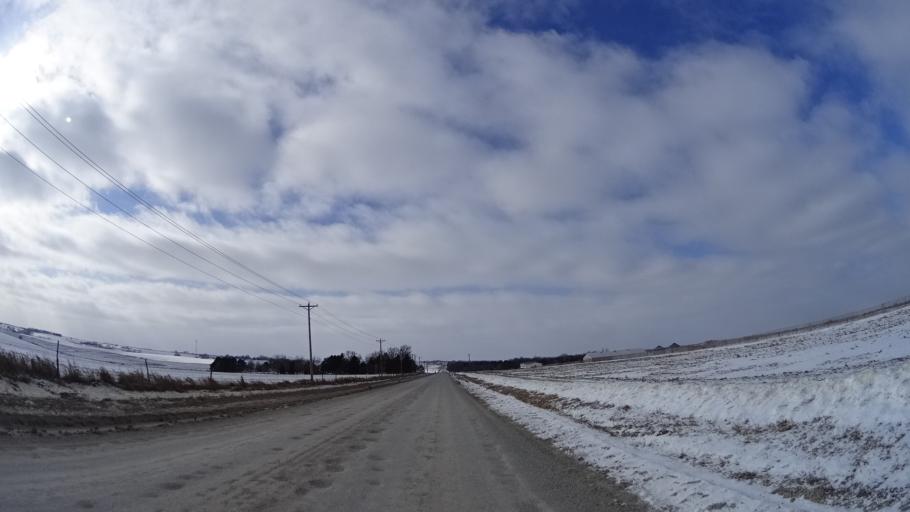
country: US
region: Nebraska
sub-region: Sarpy County
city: Papillion
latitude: 41.1181
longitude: -96.0065
